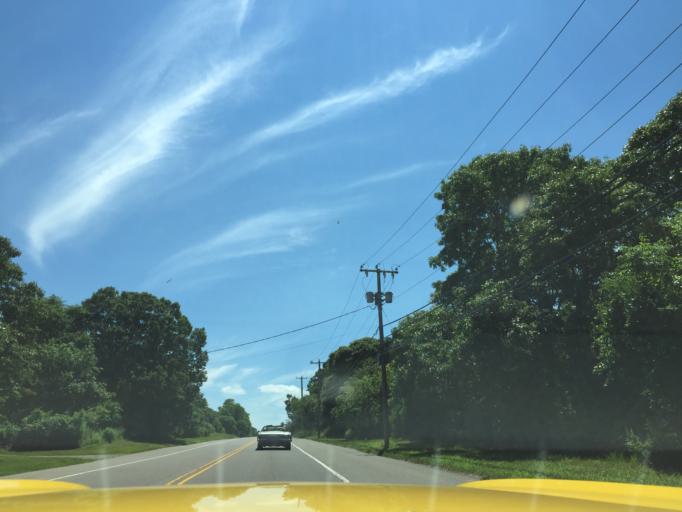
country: US
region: New York
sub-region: Suffolk County
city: Montauk
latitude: 41.0653
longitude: -71.9477
